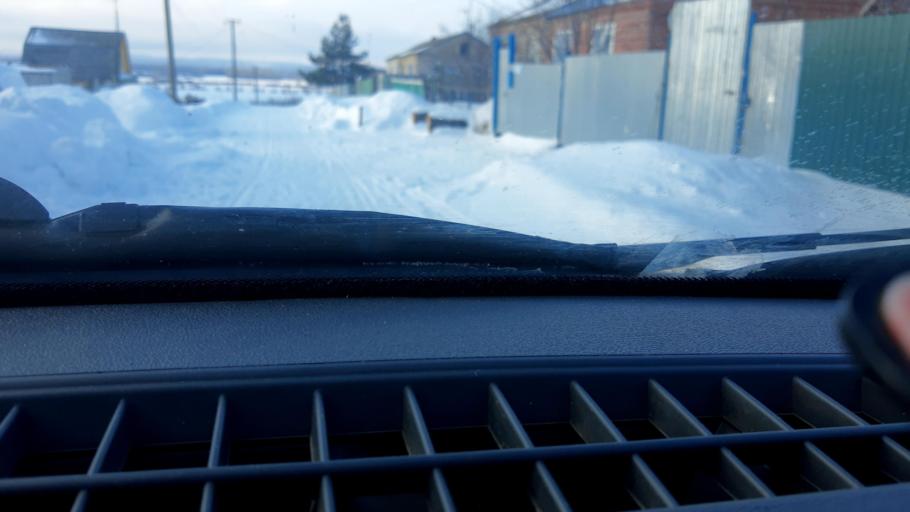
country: RU
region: Bashkortostan
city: Birsk
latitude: 55.1614
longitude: 55.6688
